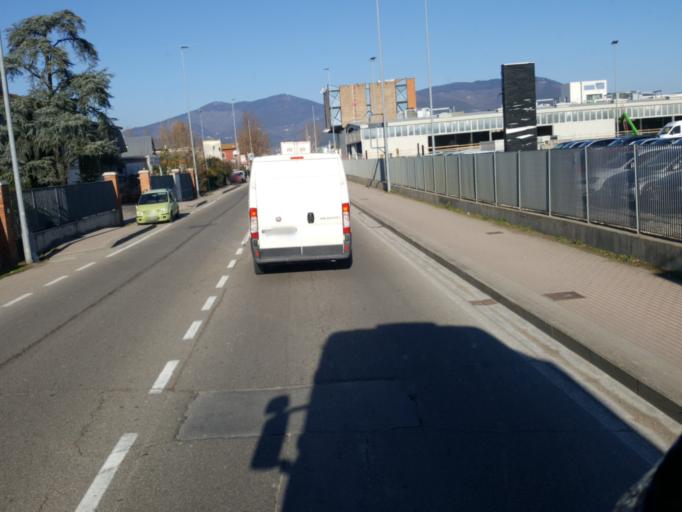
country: IT
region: Tuscany
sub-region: Province of Florence
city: Mantignano-Ugnano
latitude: 43.8047
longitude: 11.1761
